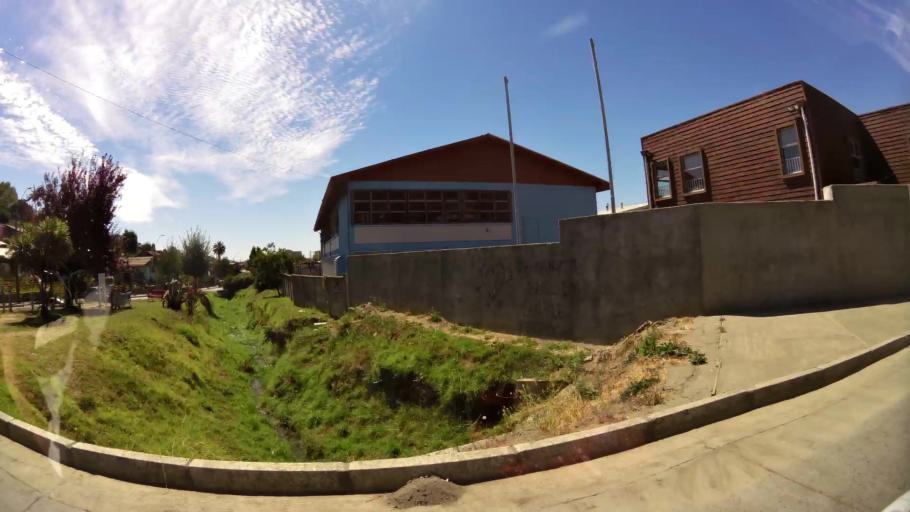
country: CL
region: Biobio
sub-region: Provincia de Concepcion
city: Penco
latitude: -36.7432
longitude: -72.9919
